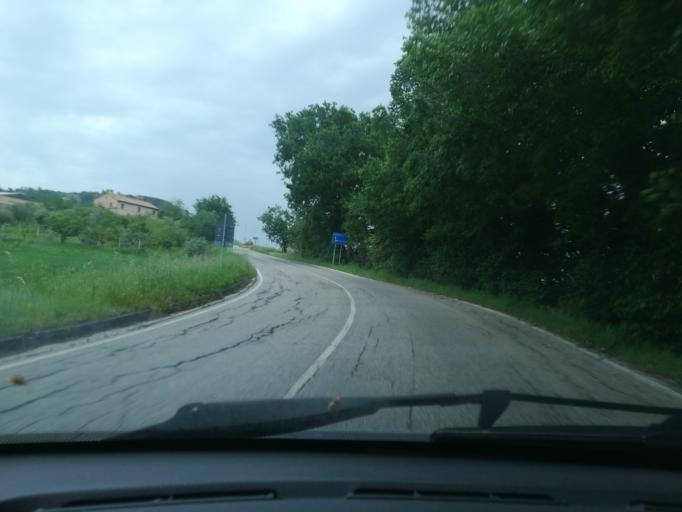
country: IT
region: The Marches
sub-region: Provincia di Macerata
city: Casette Verdini
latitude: 43.2865
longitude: 13.3923
